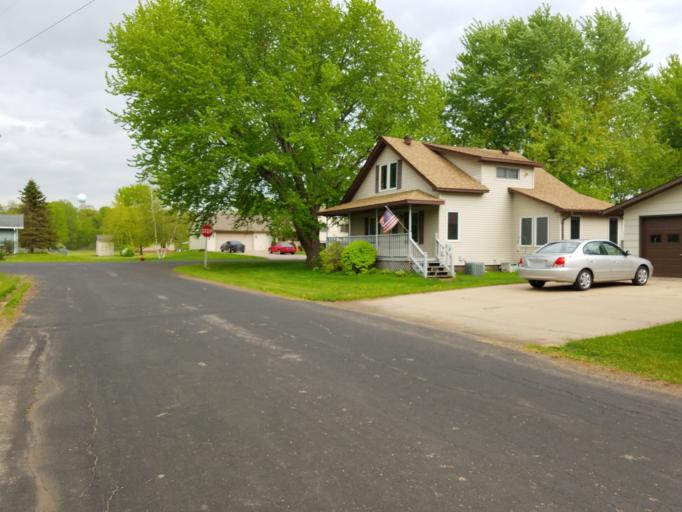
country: US
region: Wisconsin
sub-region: Dunn County
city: Menomonie
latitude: 44.7766
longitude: -91.9284
